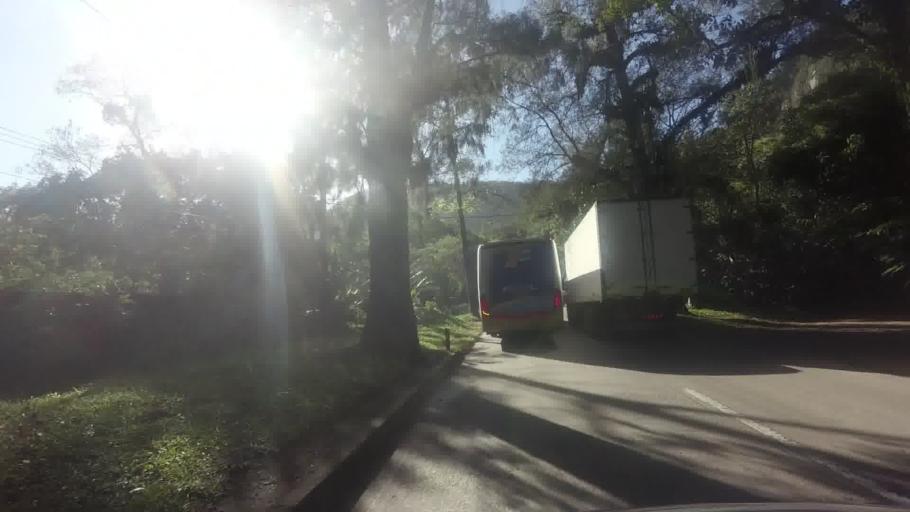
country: BR
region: Rio de Janeiro
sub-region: Petropolis
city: Petropolis
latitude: -22.5674
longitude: -43.2487
